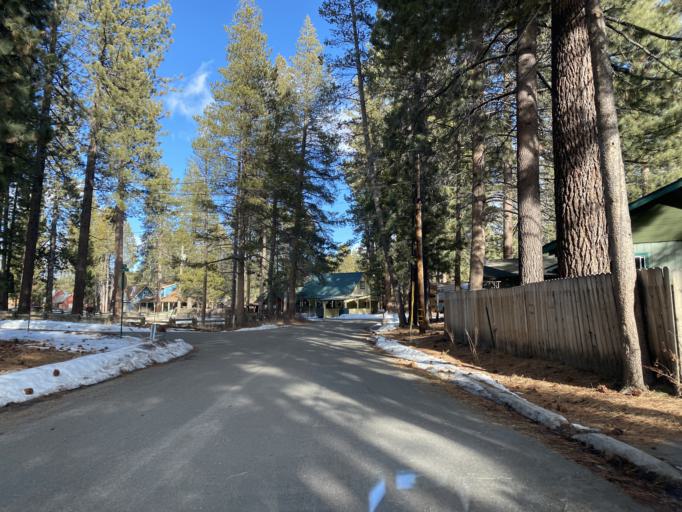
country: US
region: California
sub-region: El Dorado County
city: South Lake Tahoe
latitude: 38.9247
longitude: -119.9769
